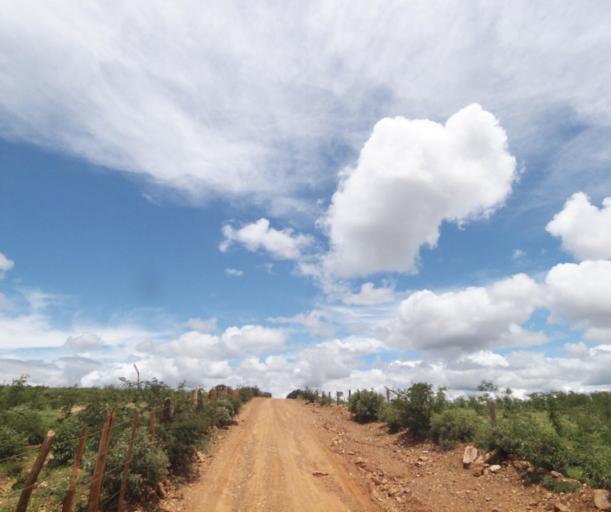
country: BR
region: Bahia
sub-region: Tanhacu
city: Tanhacu
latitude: -14.1921
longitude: -41.0627
